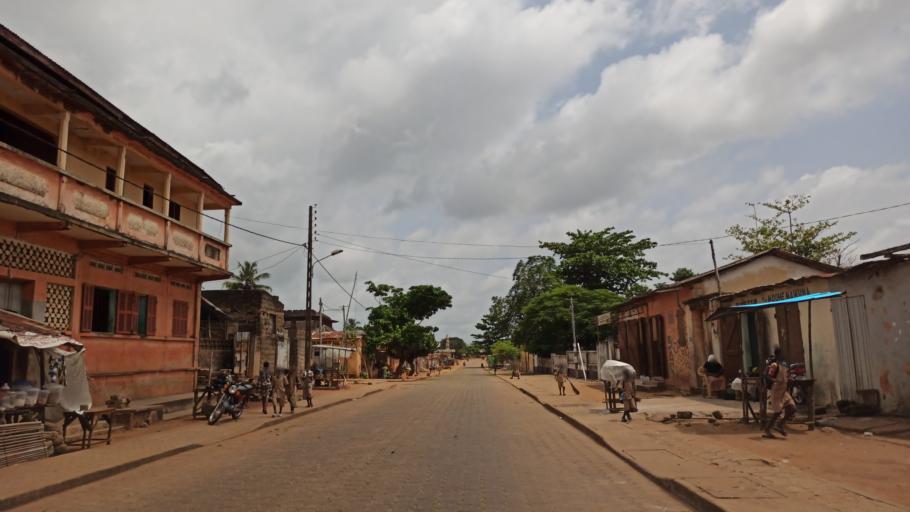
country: BJ
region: Queme
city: Porto-Novo
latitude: 6.4695
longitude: 2.6340
